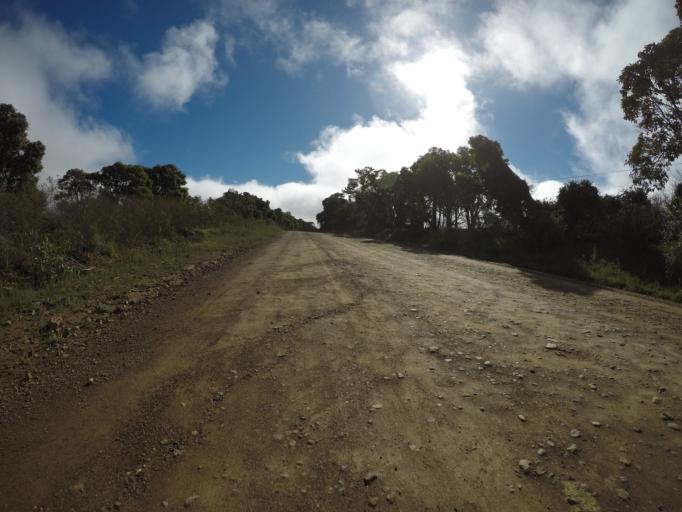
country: ZA
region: Western Cape
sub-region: Cape Winelands District Municipality
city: Ashton
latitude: -34.1176
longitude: 19.8052
